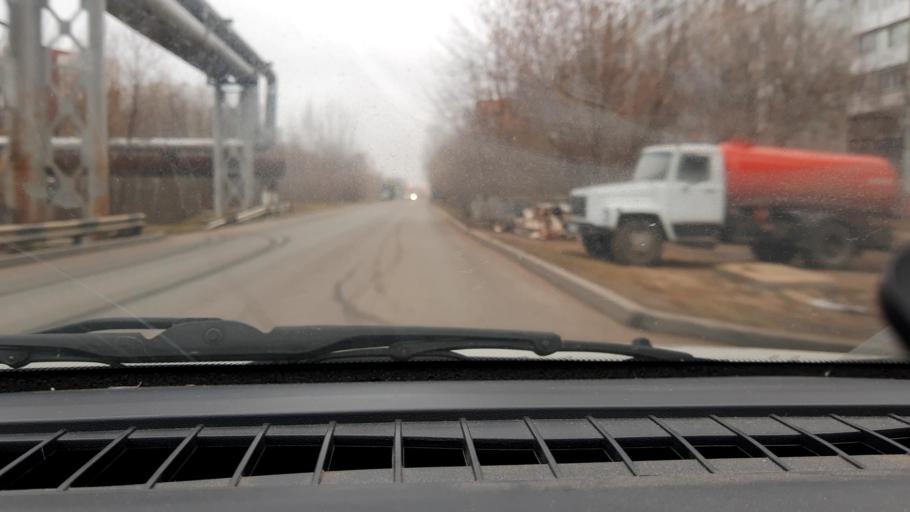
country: RU
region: Nizjnij Novgorod
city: Burevestnik
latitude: 56.2230
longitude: 43.8721
